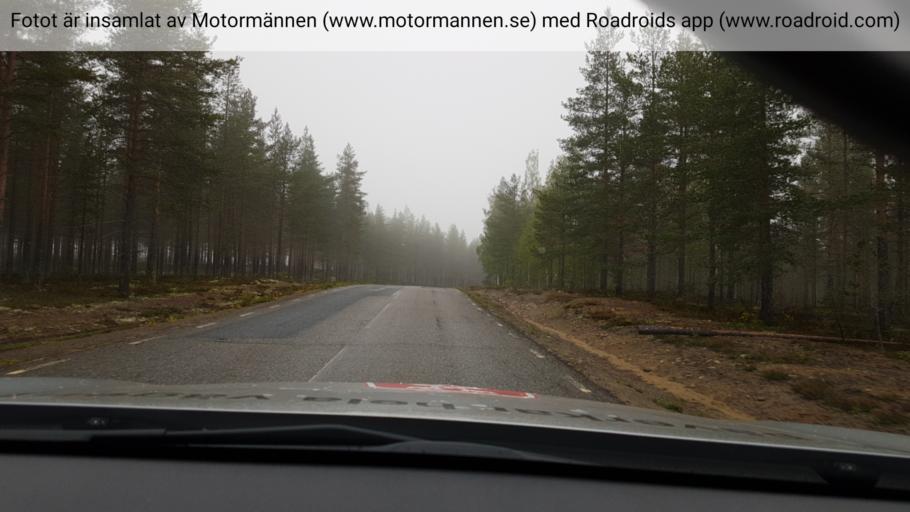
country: SE
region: Vaesterbotten
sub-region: Umea Kommun
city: Ersmark
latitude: 64.2279
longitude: 20.2828
